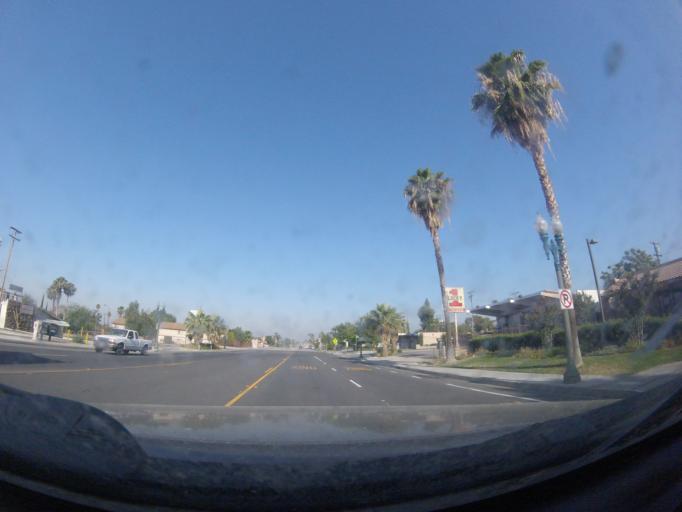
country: US
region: California
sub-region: San Bernardino County
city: Highland
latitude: 34.1213
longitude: -117.2117
